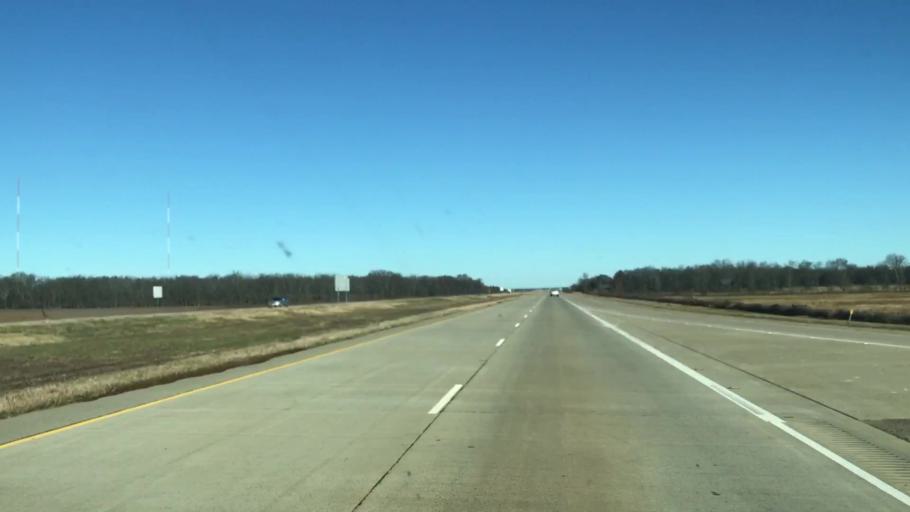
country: US
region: Louisiana
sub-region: Caddo Parish
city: Blanchard
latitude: 32.6792
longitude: -93.8518
